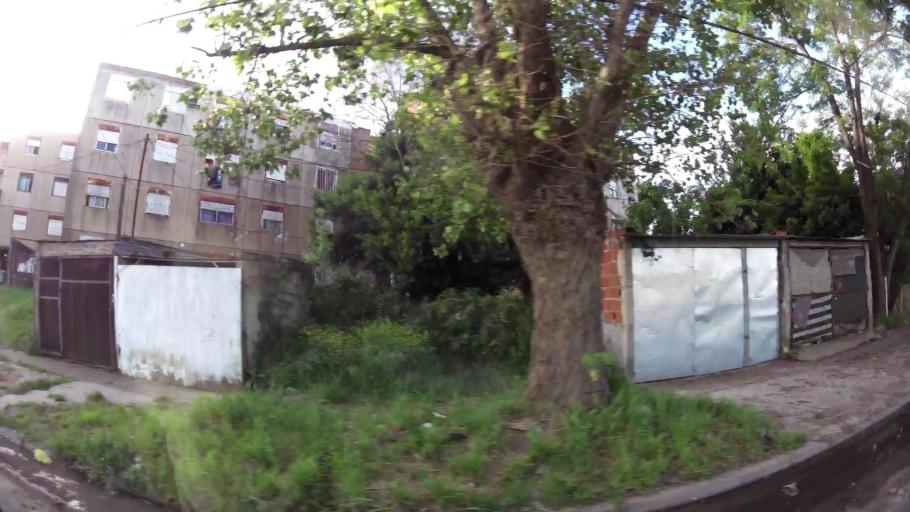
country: AR
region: Buenos Aires
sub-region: Partido de Almirante Brown
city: Adrogue
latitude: -34.8203
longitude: -58.3397
